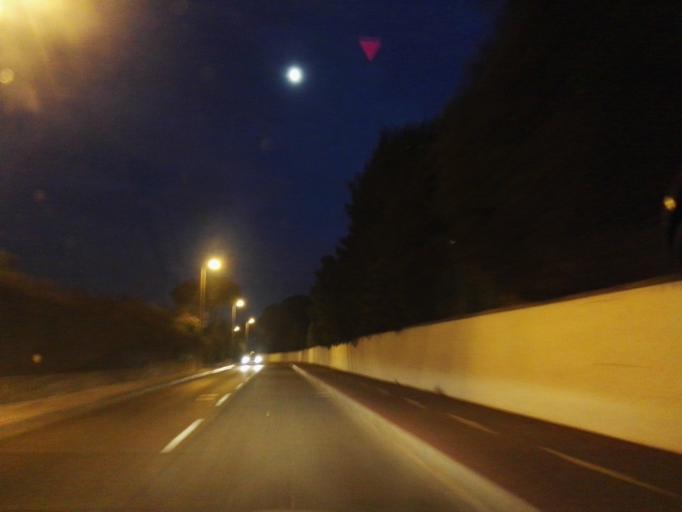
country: PT
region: Lisbon
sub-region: Cascais
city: Cascais
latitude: 38.7187
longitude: -9.4645
